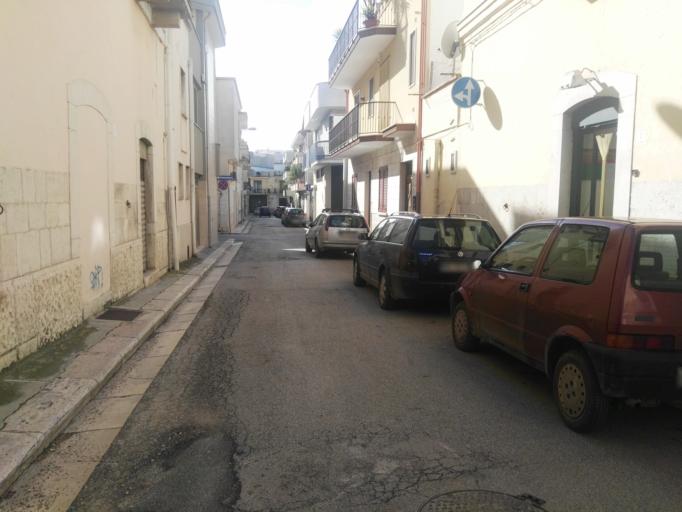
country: IT
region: Apulia
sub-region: Provincia di Barletta - Andria - Trani
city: Andria
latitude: 41.2219
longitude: 16.3017
